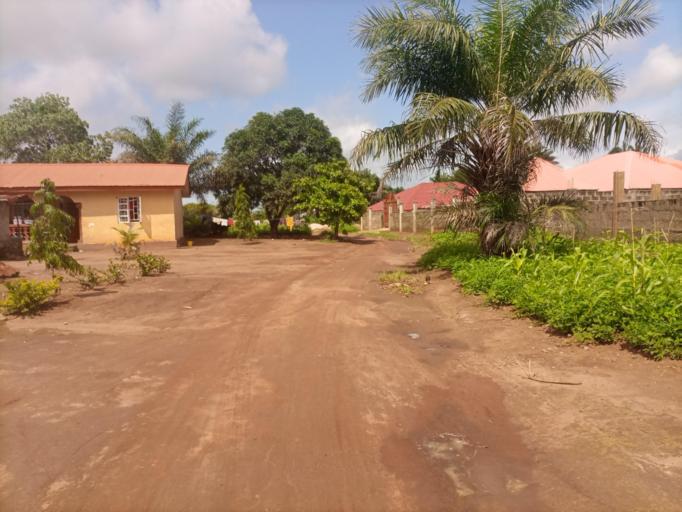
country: SL
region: Northern Province
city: Sawkta
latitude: 8.6382
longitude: -13.2108
